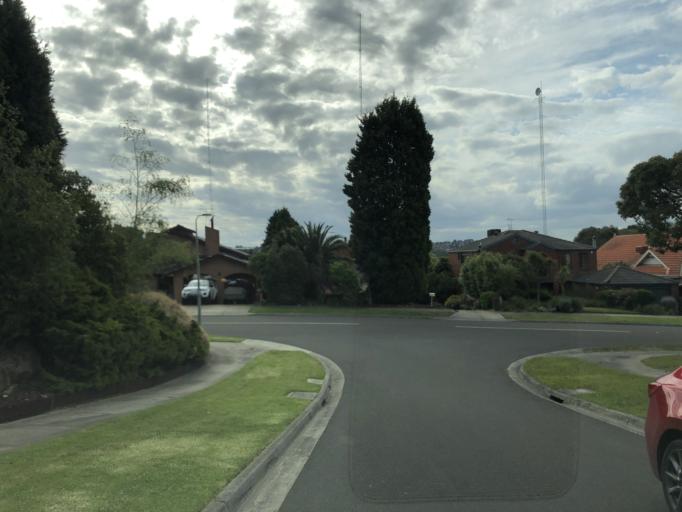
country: AU
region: Victoria
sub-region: Knox
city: Rowville
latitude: -37.9345
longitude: 145.2201
